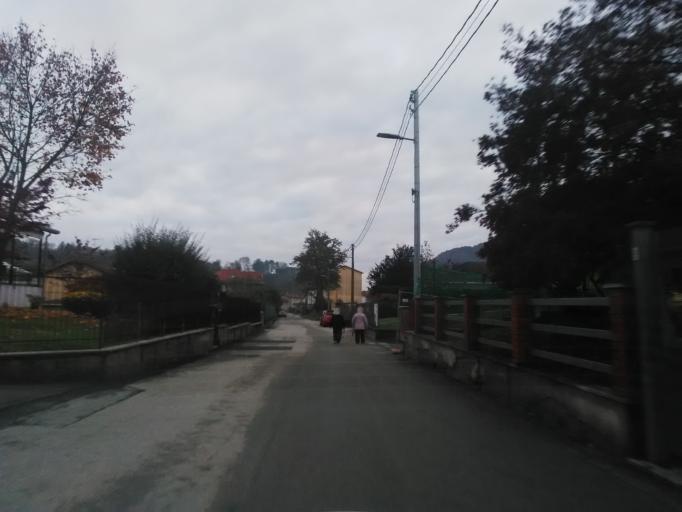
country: IT
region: Piedmont
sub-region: Provincia di Novara
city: Prato Sesia
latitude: 45.6521
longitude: 8.3776
